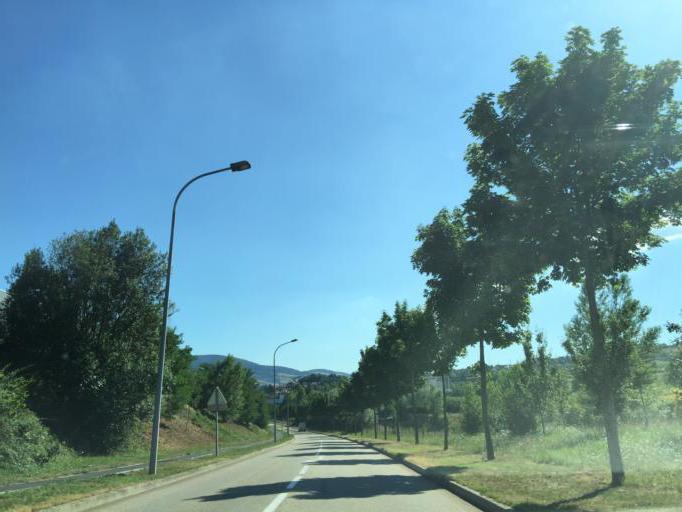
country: FR
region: Rhone-Alpes
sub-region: Departement de la Loire
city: Saint-Chamond
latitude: 45.4896
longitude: 4.5207
